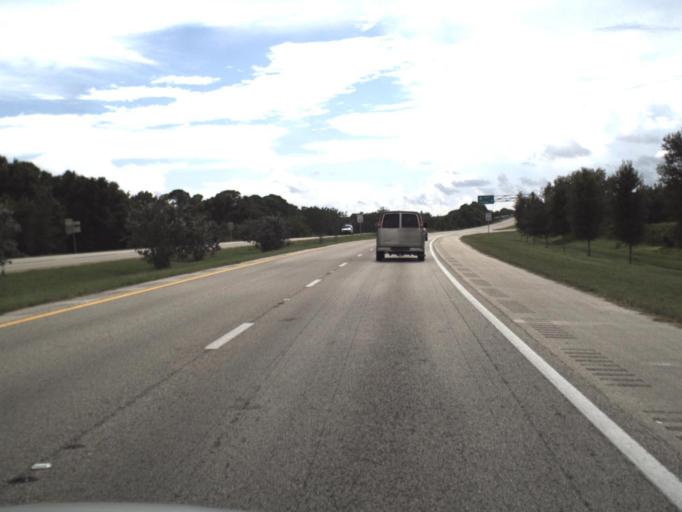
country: US
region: Florida
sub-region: Sarasota County
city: Laurel
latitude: 27.1546
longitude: -82.4602
